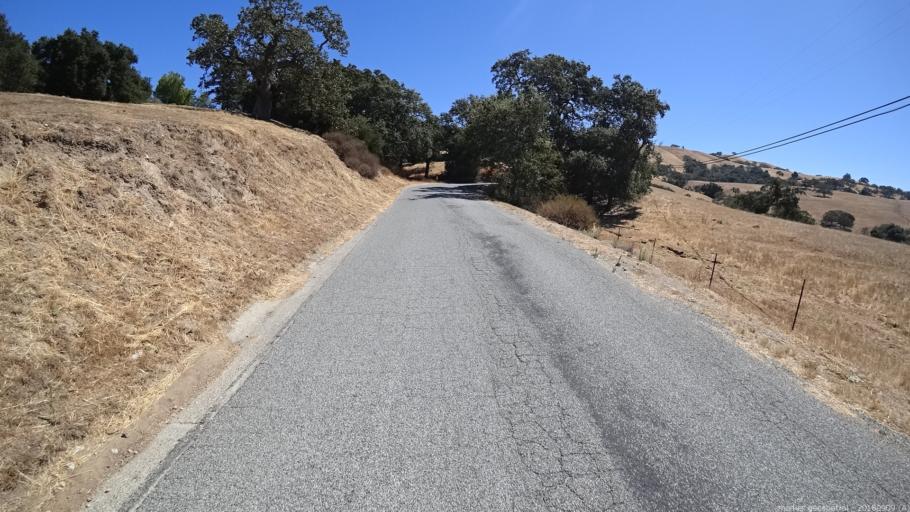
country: US
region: California
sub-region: Monterey County
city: Carmel Valley Village
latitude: 36.5409
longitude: -121.6579
